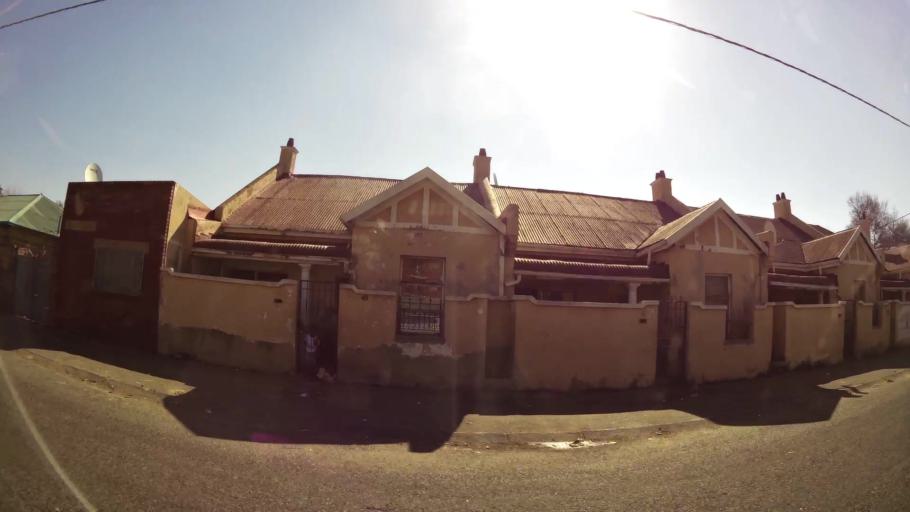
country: ZA
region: Gauteng
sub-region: City of Johannesburg Metropolitan Municipality
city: Johannesburg
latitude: -26.2015
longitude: 28.0657
